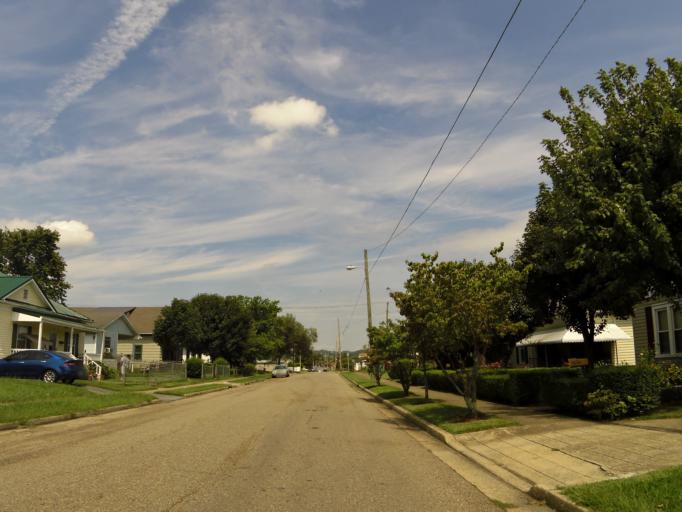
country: US
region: Tennessee
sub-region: Sullivan County
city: Kingsport
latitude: 36.5409
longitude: -82.5514
